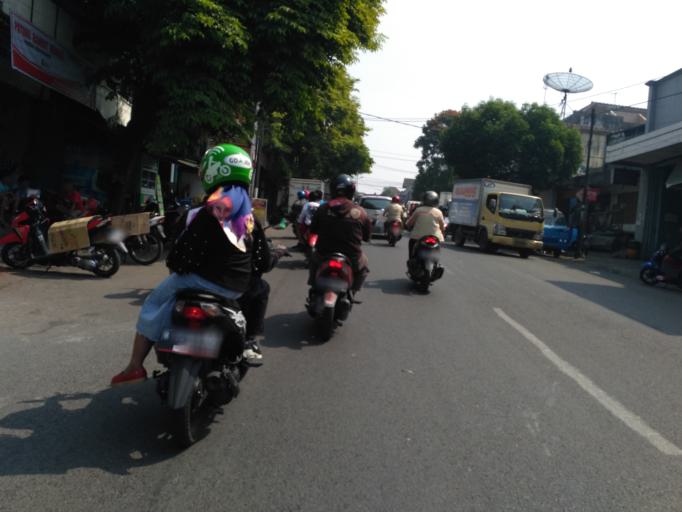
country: ID
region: East Java
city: Malang
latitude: -7.9896
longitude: 112.6394
